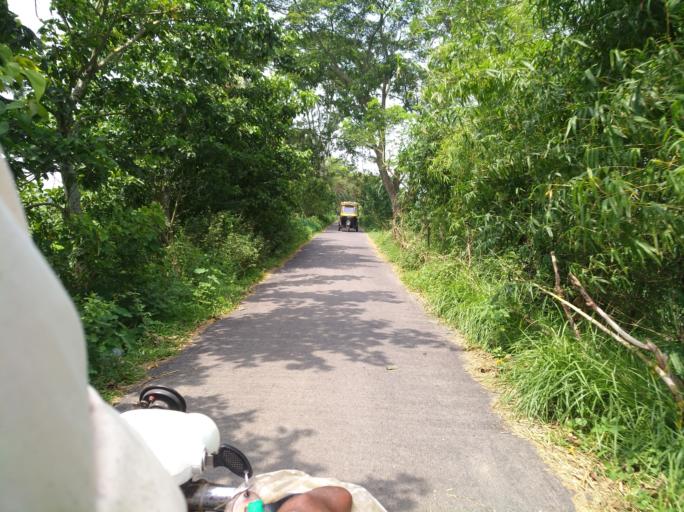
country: BD
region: Dhaka
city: Palang
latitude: 23.2478
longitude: 90.3083
